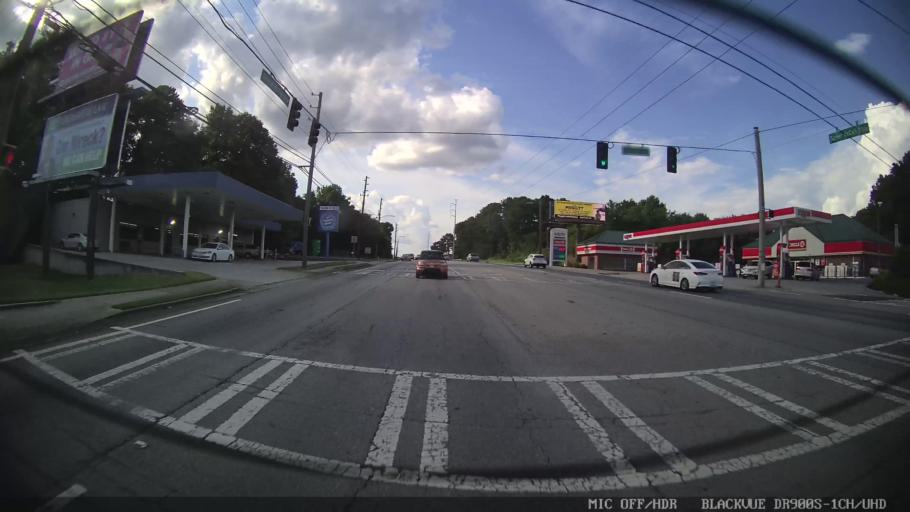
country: US
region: Georgia
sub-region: Floyd County
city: Rome
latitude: 34.2468
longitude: -85.1615
